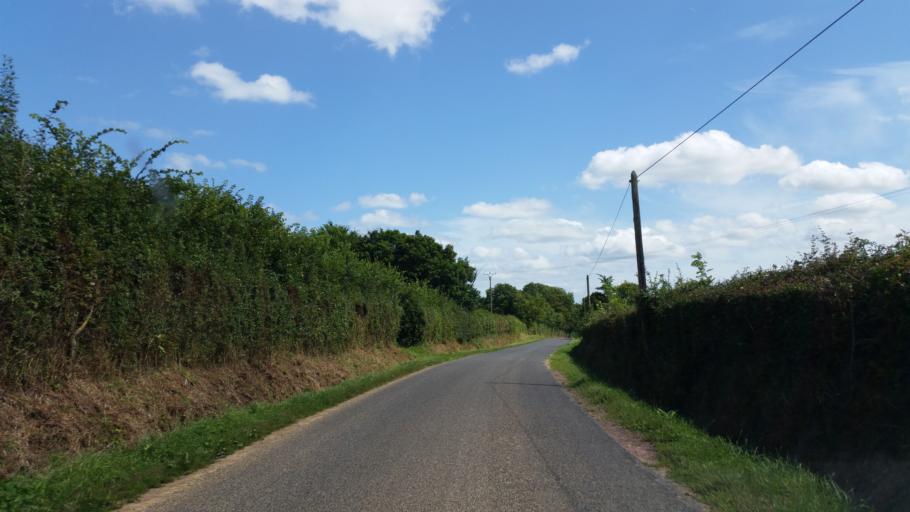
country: FR
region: Lower Normandy
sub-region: Departement de la Manche
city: Montebourg
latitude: 49.4644
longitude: -1.3351
